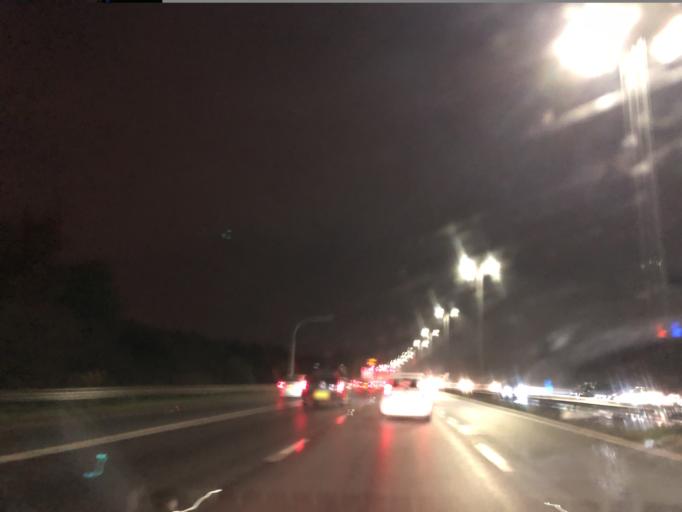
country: GB
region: England
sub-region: Walsall
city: Bloxwich
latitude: 52.6051
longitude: -2.0196
